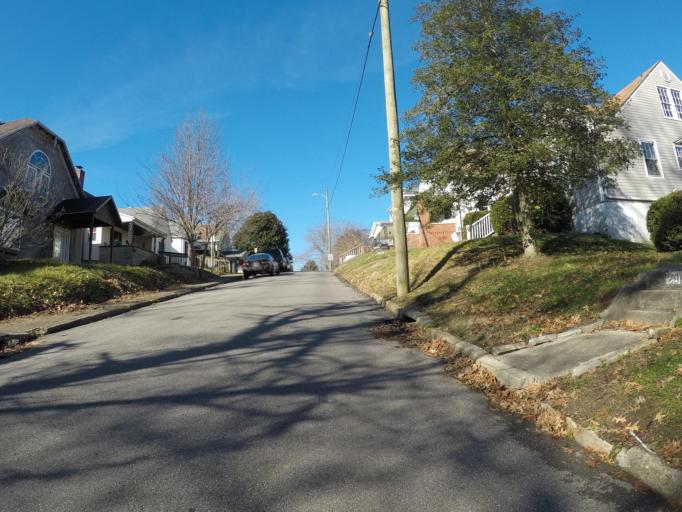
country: US
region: West Virginia
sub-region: Cabell County
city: Huntington
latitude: 38.4078
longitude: -82.4064
